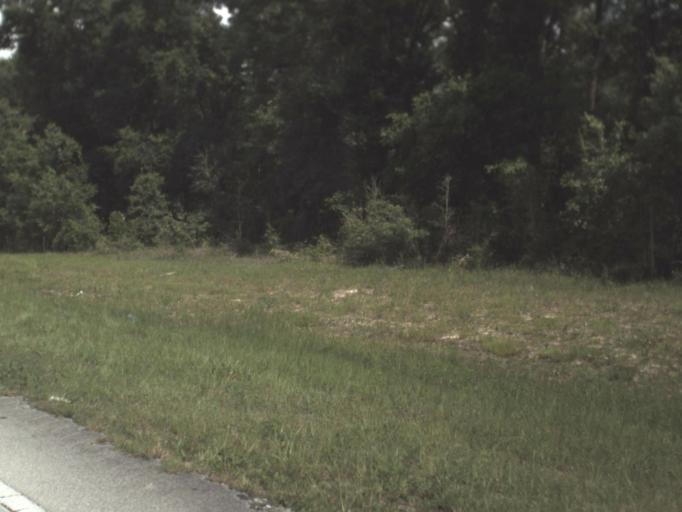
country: US
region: Florida
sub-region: Bradford County
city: Starke
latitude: 29.9820
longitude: -82.0033
